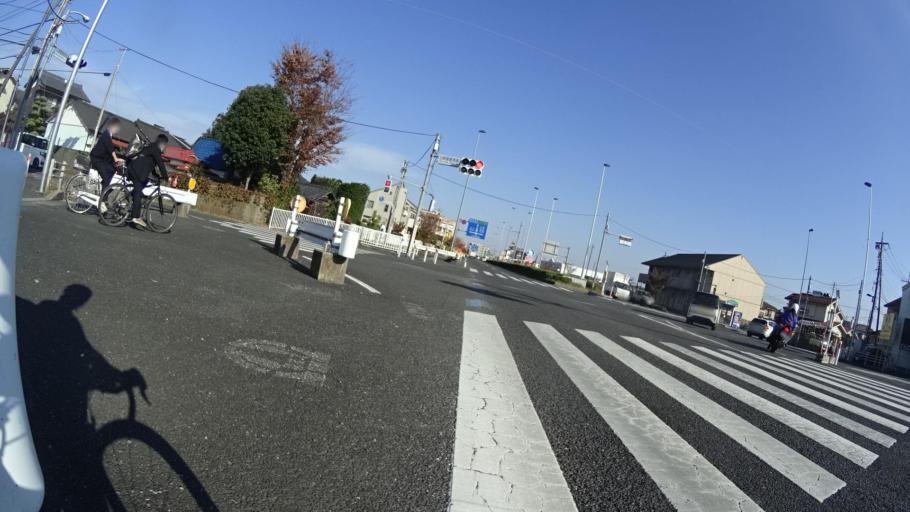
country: JP
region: Tokyo
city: Kokubunji
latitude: 35.6747
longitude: 139.4681
